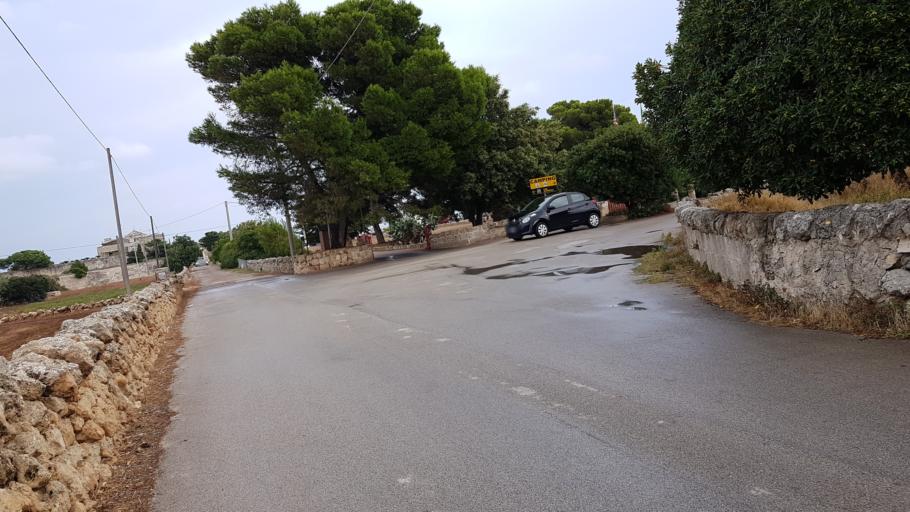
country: IT
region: Apulia
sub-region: Provincia di Bari
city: Monopoli
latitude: 40.9286
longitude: 17.3290
